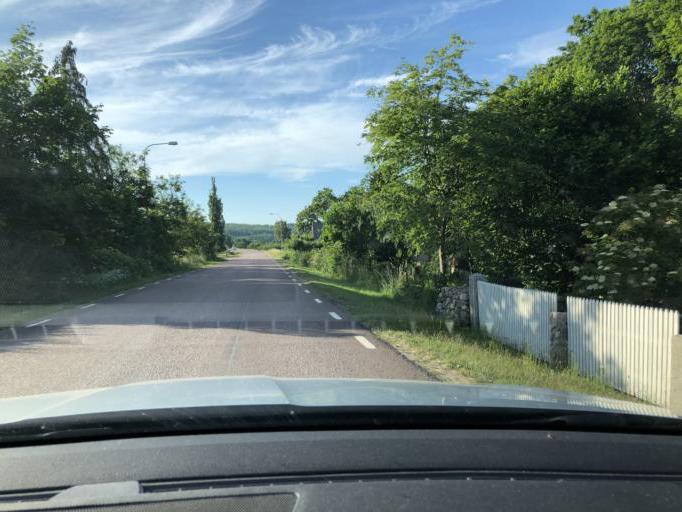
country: SE
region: Blekinge
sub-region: Solvesborgs Kommun
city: Soelvesborg
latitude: 56.1525
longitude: 14.6029
